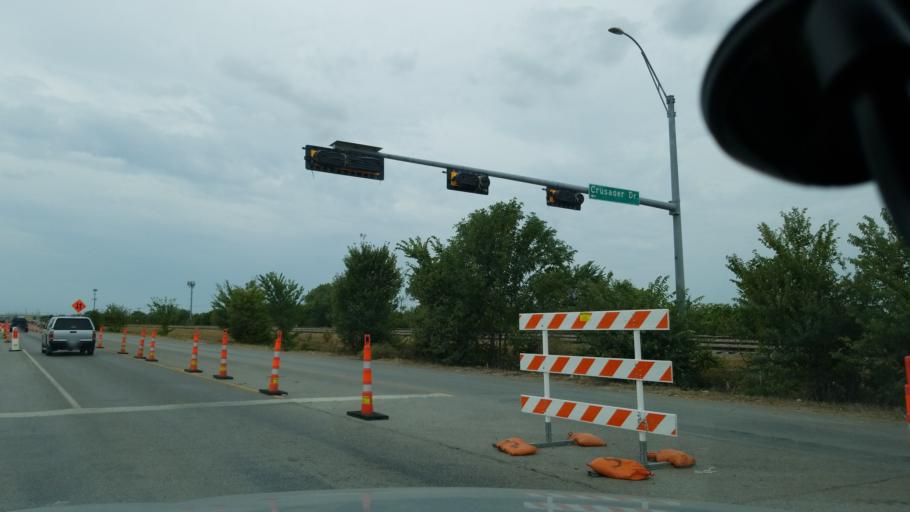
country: US
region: Texas
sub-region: Dallas County
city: Grand Prairie
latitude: 32.7454
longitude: -96.9802
